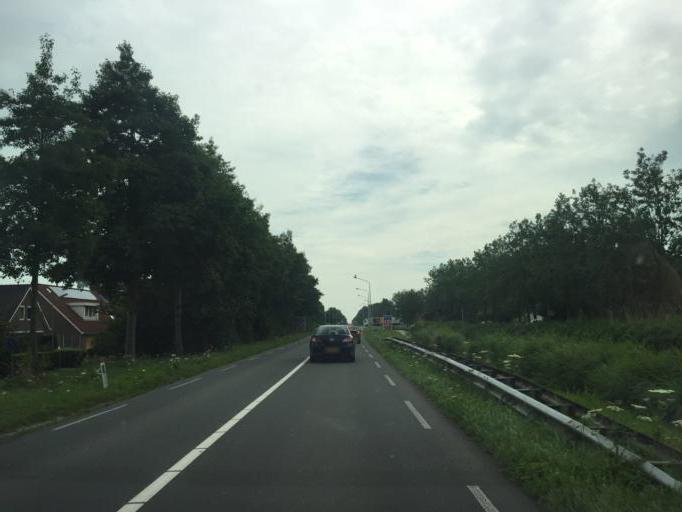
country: NL
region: North Holland
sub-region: Gemeente Langedijk
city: Broek op Langedijk
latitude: 52.6126
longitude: 4.8161
